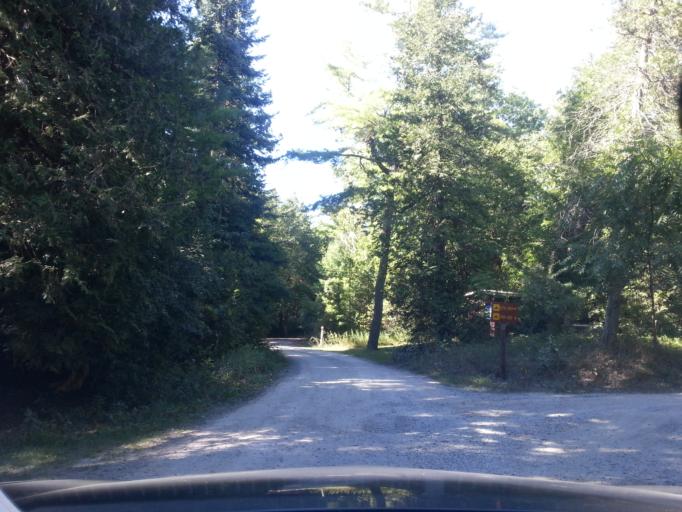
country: CA
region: Ontario
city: Prince Edward
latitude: 43.9021
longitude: -77.2287
